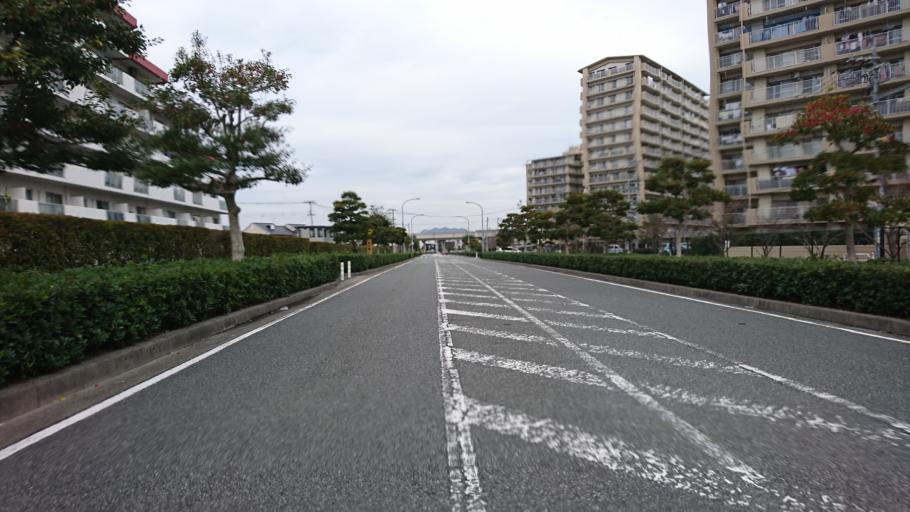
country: JP
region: Hyogo
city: Kakogawacho-honmachi
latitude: 34.7608
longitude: 134.8457
